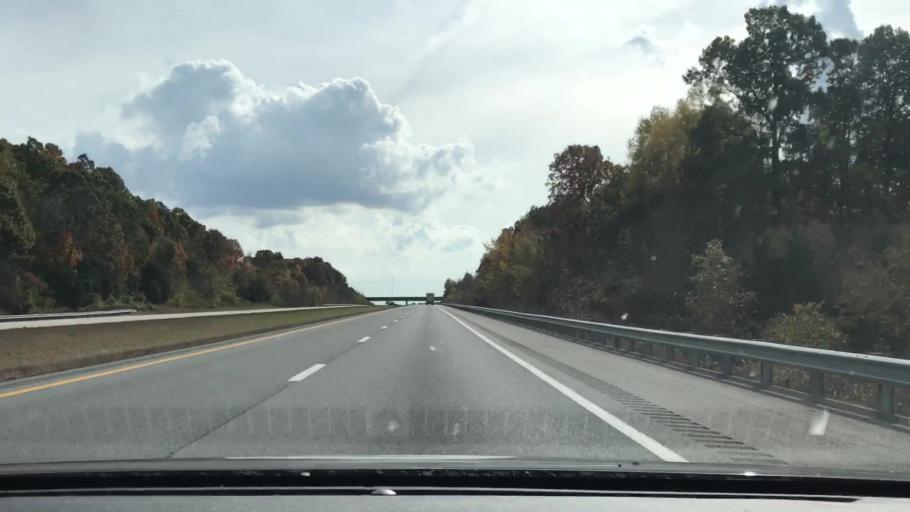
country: US
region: Kentucky
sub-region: Lyon County
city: Eddyville
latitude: 37.0125
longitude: -87.9774
